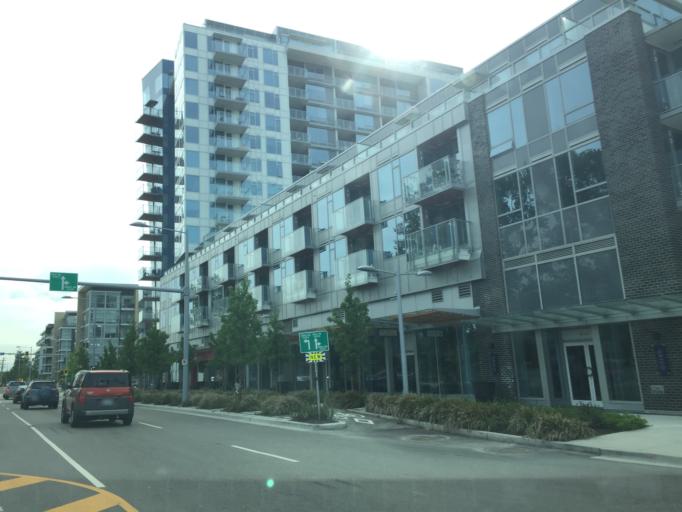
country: CA
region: British Columbia
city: Richmond
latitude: 49.1755
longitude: -123.1472
